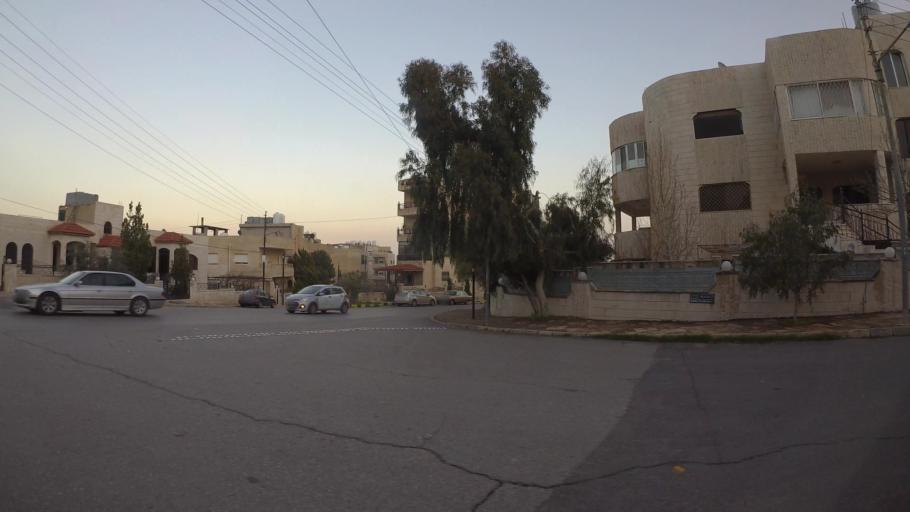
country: JO
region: Amman
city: Amman
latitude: 31.9970
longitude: 35.9516
